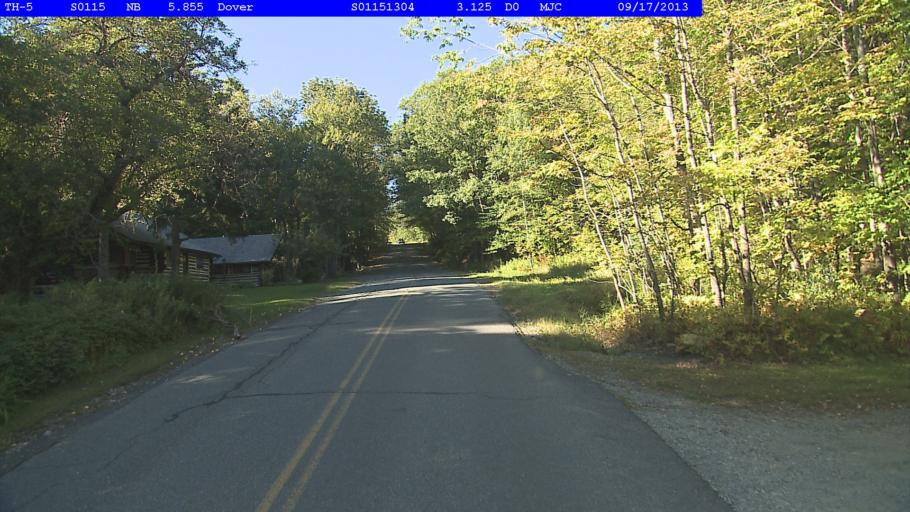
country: US
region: Vermont
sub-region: Windham County
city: Dover
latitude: 42.9690
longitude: -72.8900
